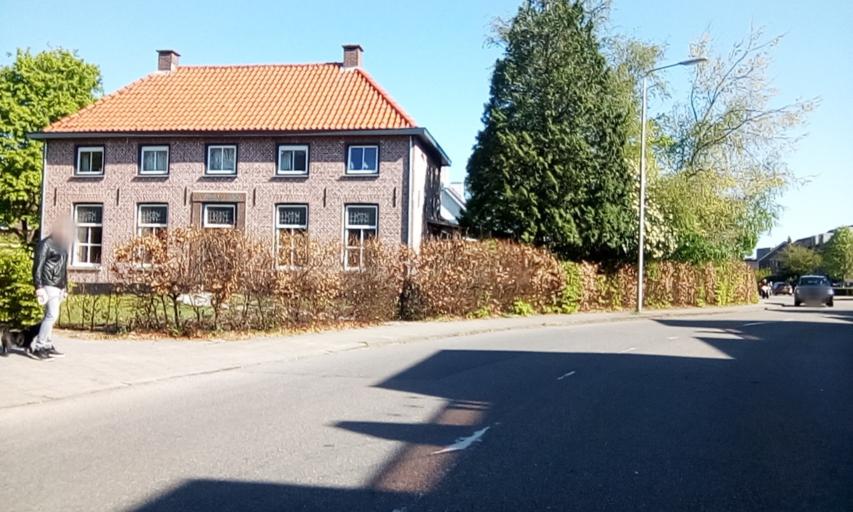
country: NL
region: Gelderland
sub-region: Gemeente Druten
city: Druten
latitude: 51.8887
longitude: 5.6053
